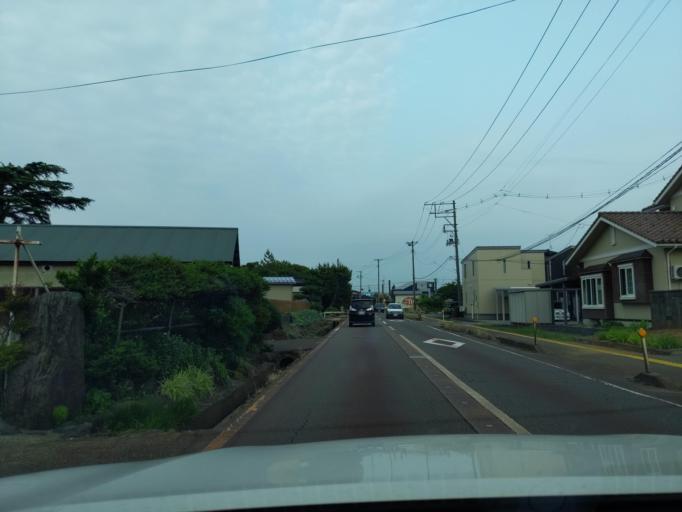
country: JP
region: Niigata
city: Kashiwazaki
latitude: 37.3881
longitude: 138.5813
